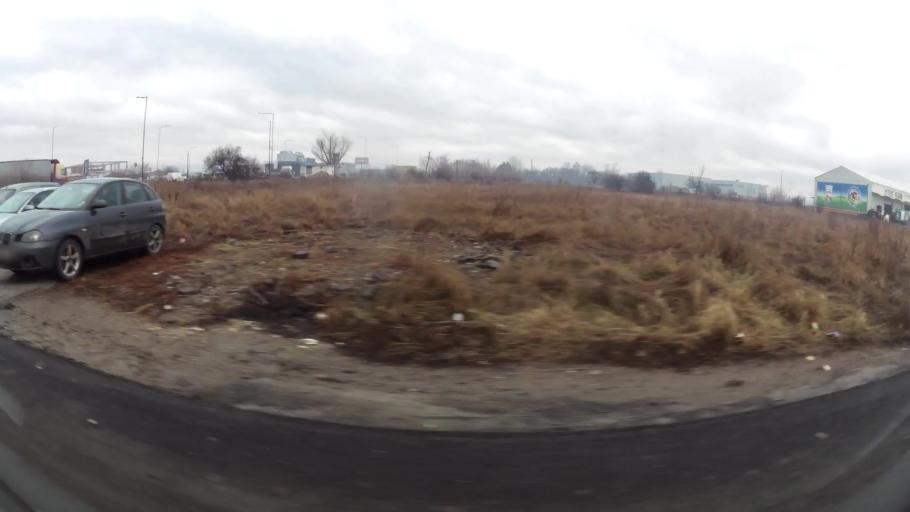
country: BG
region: Sofia-Capital
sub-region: Stolichna Obshtina
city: Sofia
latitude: 42.7086
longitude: 23.4294
